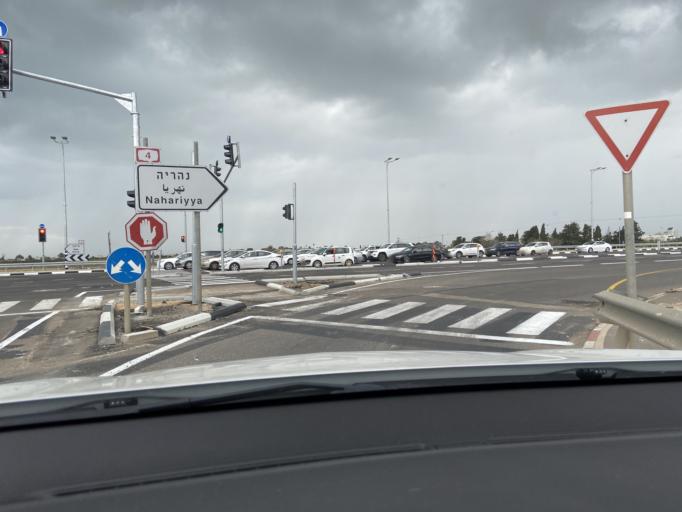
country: IL
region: Northern District
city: El Mazra`a
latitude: 32.9780
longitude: 35.0941
